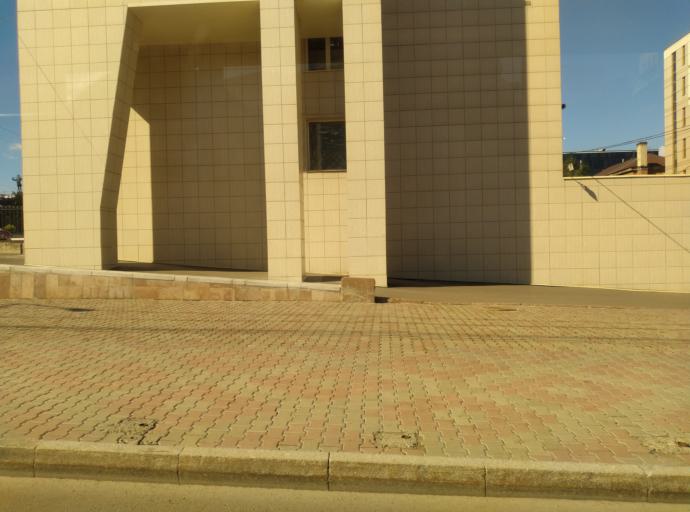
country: RU
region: Krasnoyarskiy
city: Krasnoyarsk
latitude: 56.0095
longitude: 92.8712
